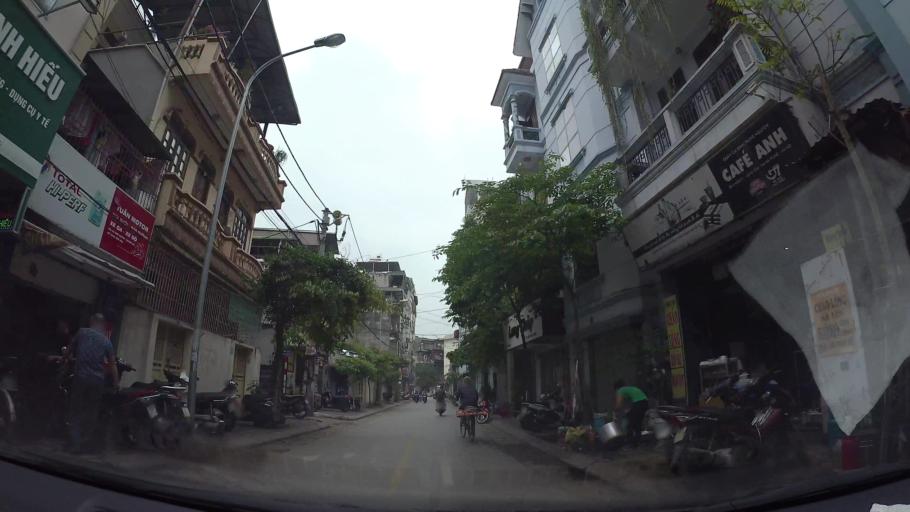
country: VN
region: Ha Noi
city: Hai BaTrung
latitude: 21.0010
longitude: 105.8582
